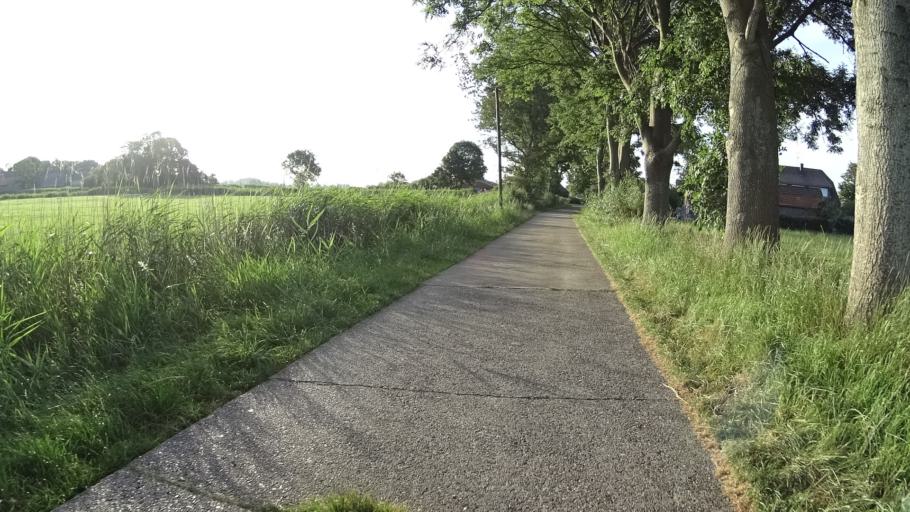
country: DE
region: Lower Saxony
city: Butjadingen
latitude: 53.6036
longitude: 8.2789
